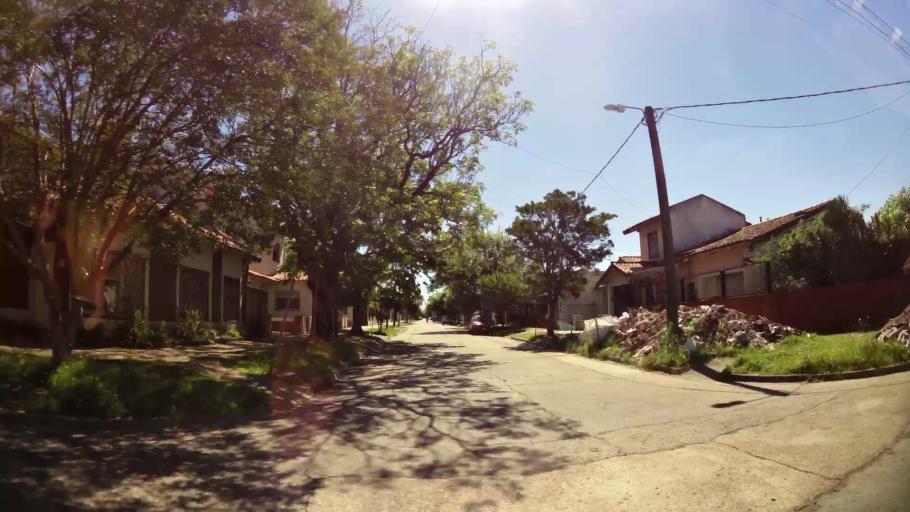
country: AR
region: Buenos Aires
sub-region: Partido de Lomas de Zamora
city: Lomas de Zamora
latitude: -34.7363
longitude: -58.4104
